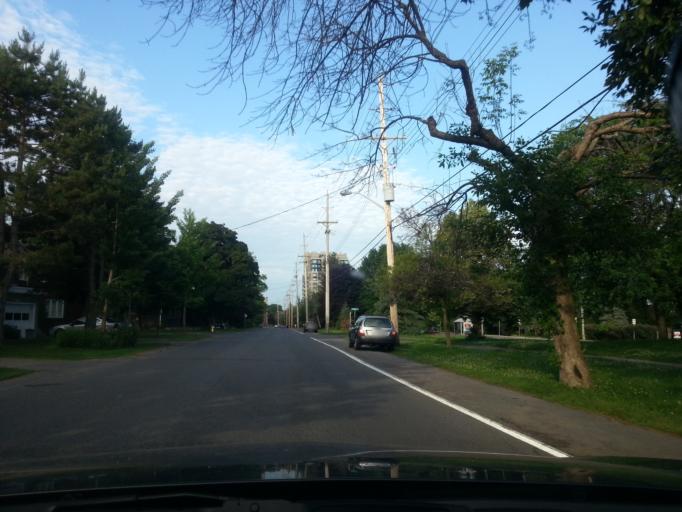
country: CA
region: Ontario
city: Ottawa
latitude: 45.3843
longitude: -75.7666
